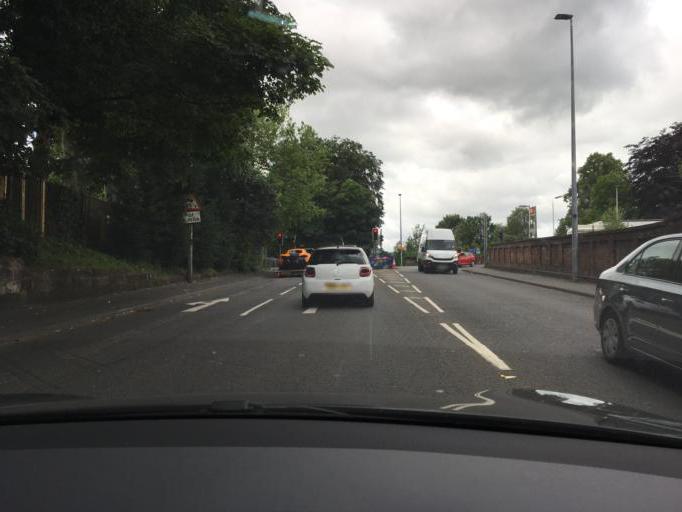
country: GB
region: England
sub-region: Cheshire East
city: Knutsford
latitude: 53.3014
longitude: -2.3719
